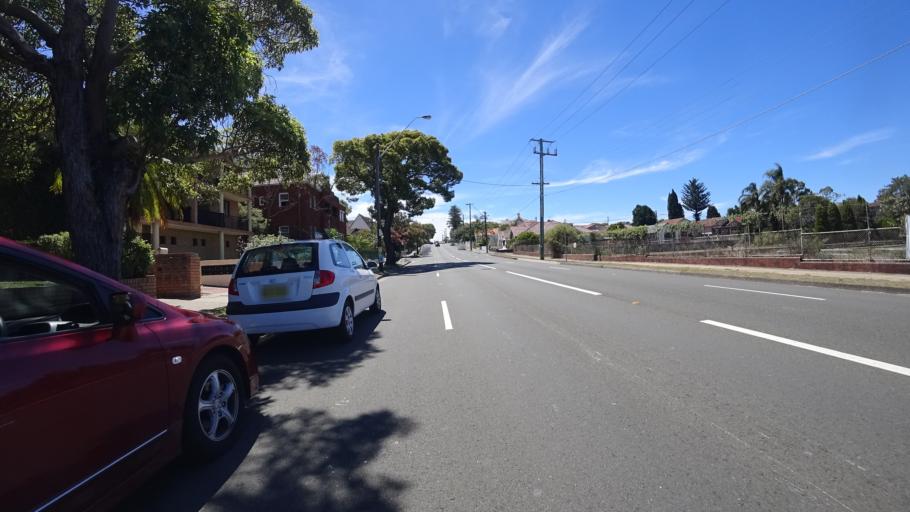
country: AU
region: New South Wales
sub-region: Rockdale
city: Banksia
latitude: -33.9517
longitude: 151.1309
